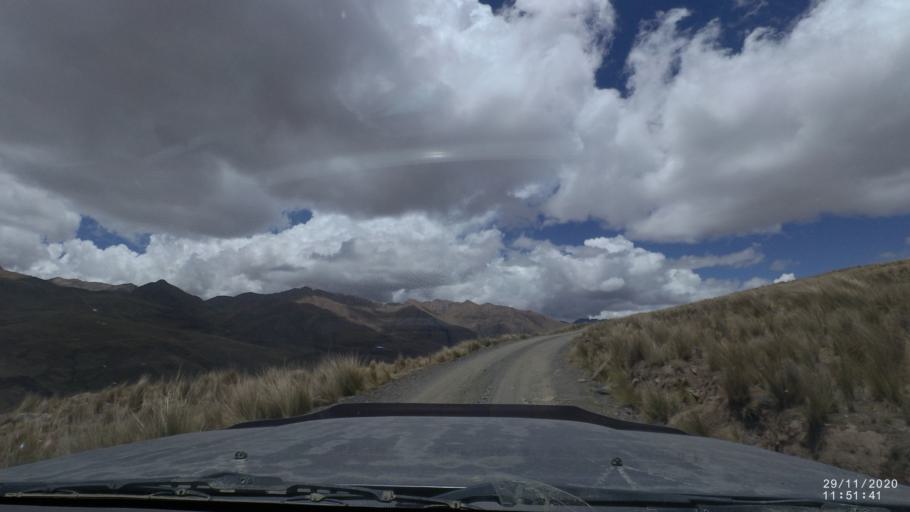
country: BO
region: Cochabamba
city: Cochabamba
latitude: -17.1726
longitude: -66.2630
